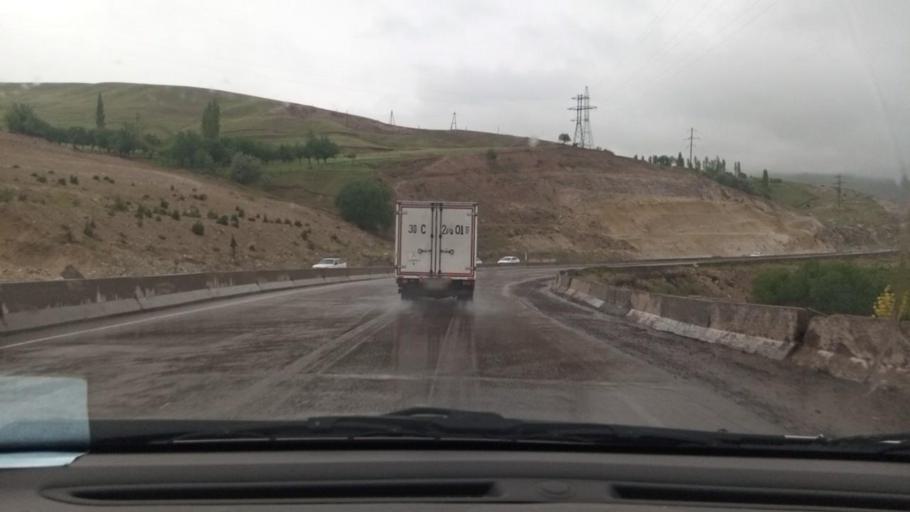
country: UZ
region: Toshkent
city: Angren
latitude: 41.0702
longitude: 70.2429
